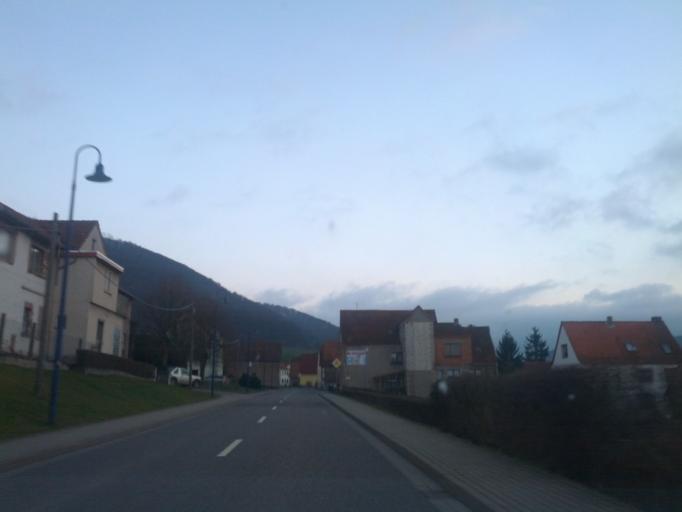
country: DE
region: Thuringia
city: Treffurt
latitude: 51.1080
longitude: 10.2212
